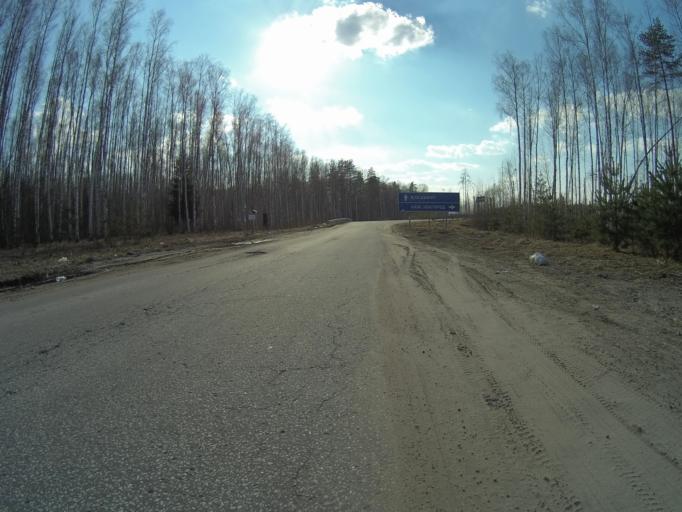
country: RU
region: Vladimir
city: Sudogda
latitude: 56.1025
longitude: 40.7756
